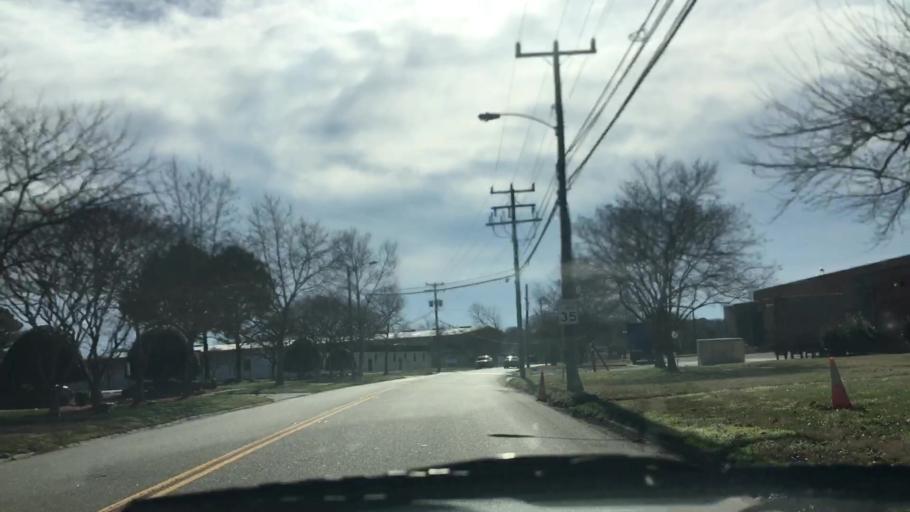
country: US
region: Virginia
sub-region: City of Norfolk
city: Norfolk
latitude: 36.8611
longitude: -76.2337
